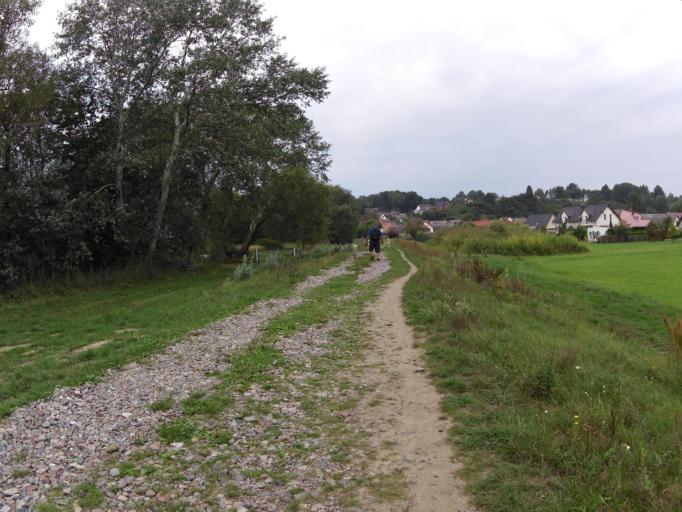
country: PL
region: West Pomeranian Voivodeship
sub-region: Swinoujscie
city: Swinoujscie
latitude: 53.8677
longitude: 14.2110
